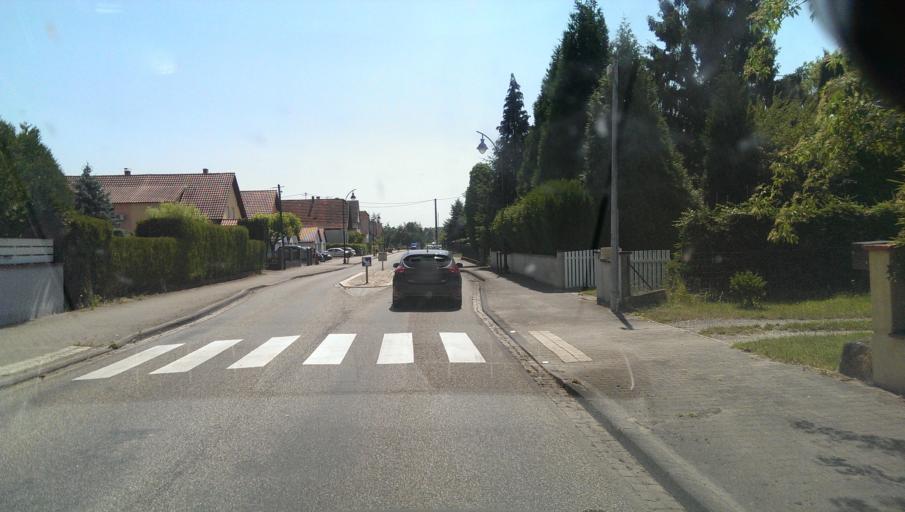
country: FR
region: Alsace
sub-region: Departement du Bas-Rhin
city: Roppenheim
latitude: 48.8600
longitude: 8.0827
